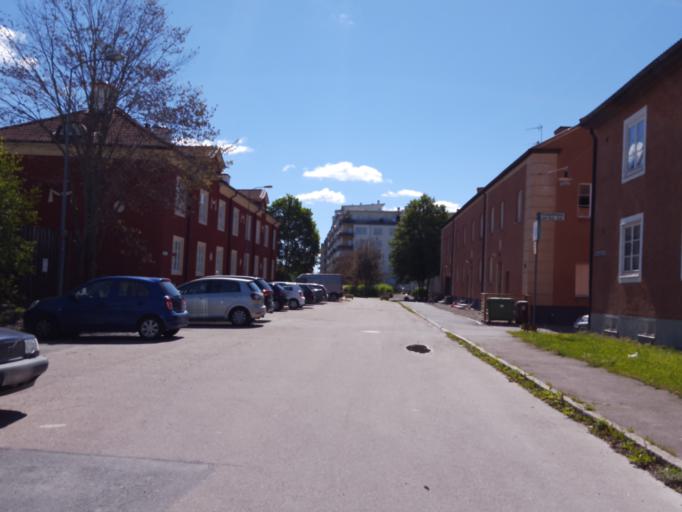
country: SE
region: Uppsala
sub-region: Uppsala Kommun
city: Uppsala
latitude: 59.8525
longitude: 17.6514
